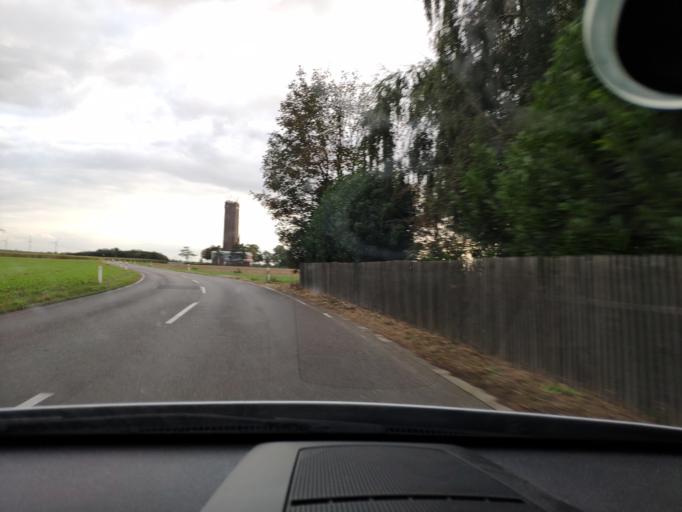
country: DE
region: North Rhine-Westphalia
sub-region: Regierungsbezirk Koln
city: Heinsberg
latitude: 51.0459
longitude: 6.1332
